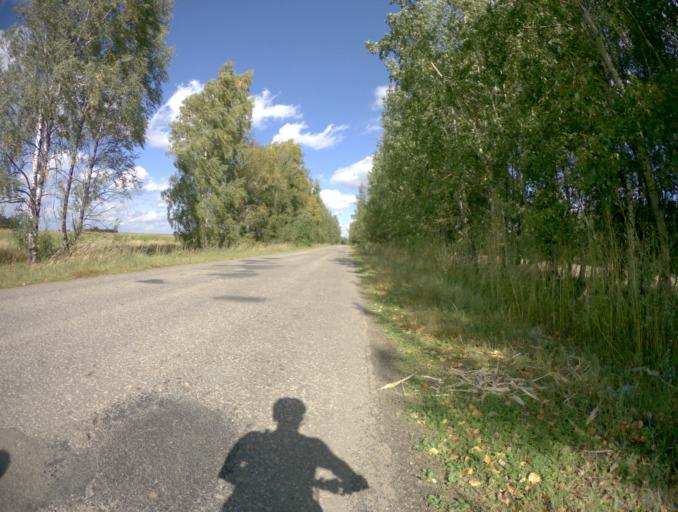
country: RU
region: Vladimir
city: Lakinsk
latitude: 55.9101
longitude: 39.8917
